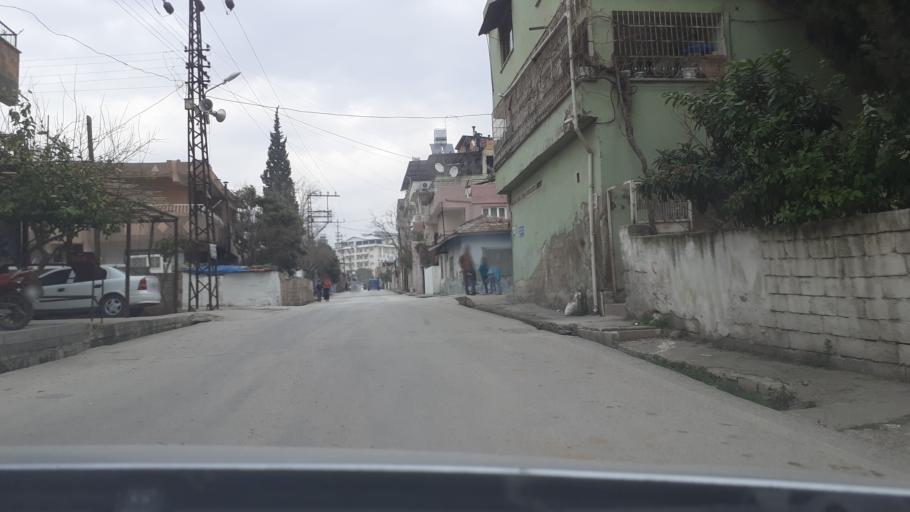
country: TR
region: Hatay
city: Kirikhan
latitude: 36.4950
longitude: 36.3512
